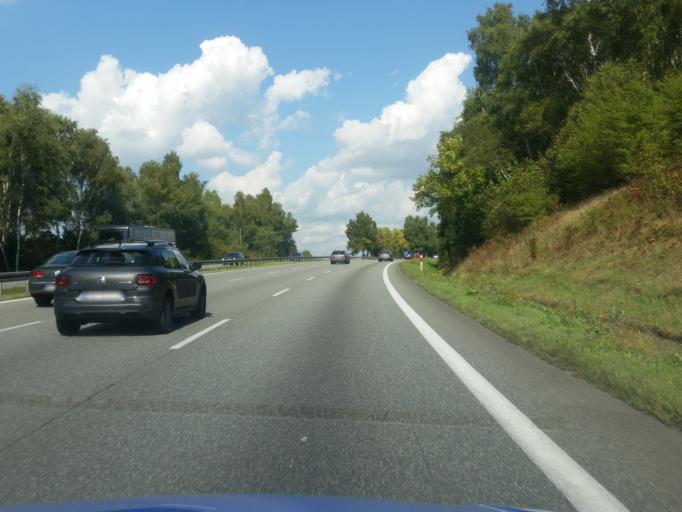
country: PL
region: Silesian Voivodeship
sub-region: Powiat bedzinski
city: Siewierz
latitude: 50.4357
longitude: 19.2152
